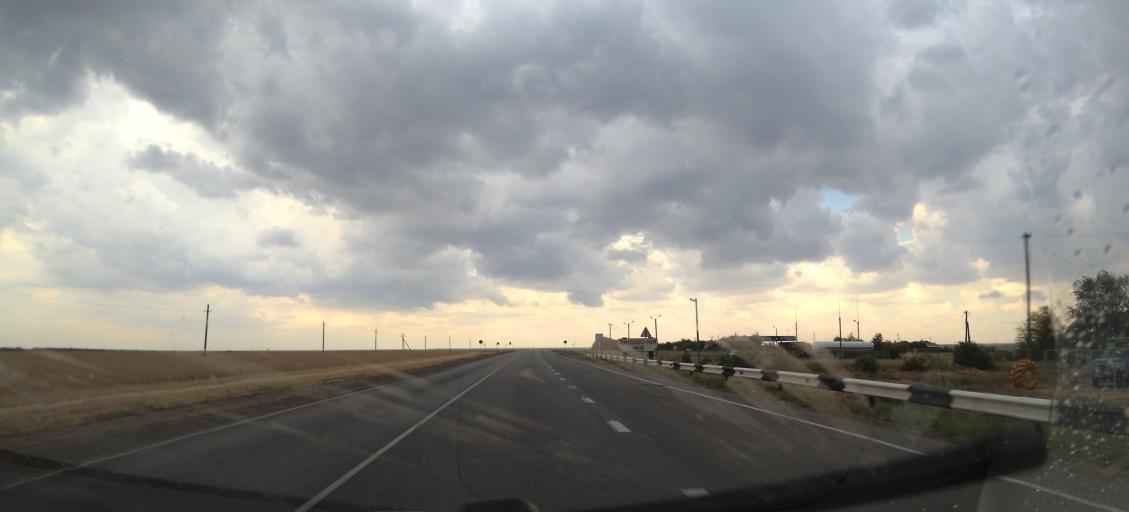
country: RU
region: Rostov
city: Orlovskiy
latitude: 46.8773
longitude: 42.0011
